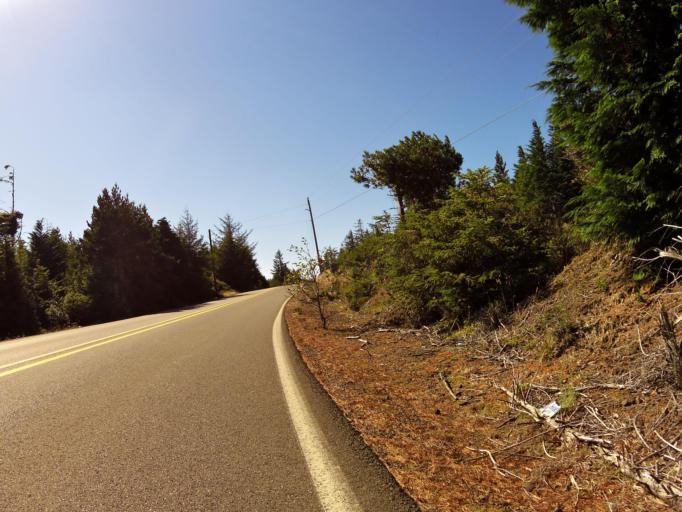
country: US
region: Oregon
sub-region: Coos County
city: Barview
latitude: 43.2765
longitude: -124.3546
